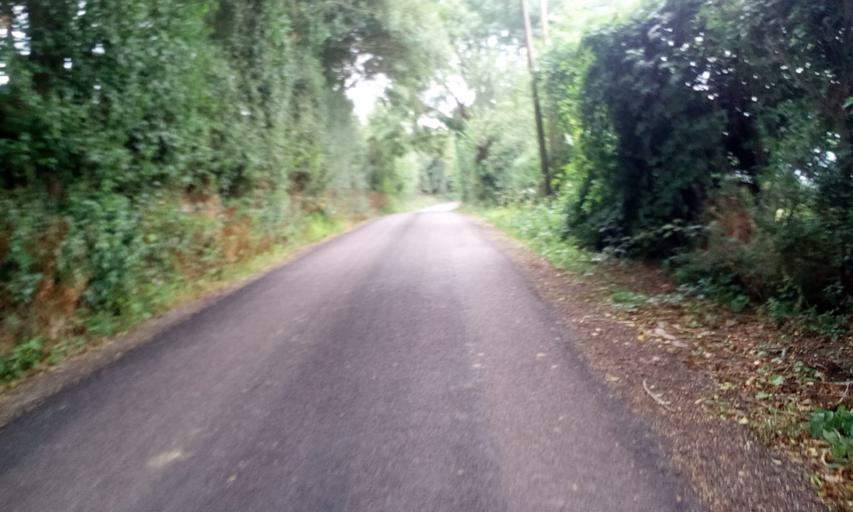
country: FR
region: Lower Normandy
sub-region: Departement du Calvados
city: Troarn
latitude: 49.1995
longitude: -0.1506
